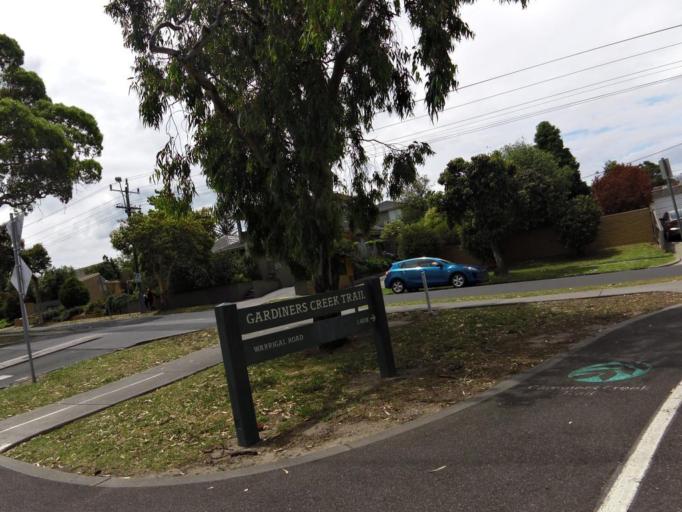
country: AU
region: Victoria
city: Ashburton
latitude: -37.8695
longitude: 145.0794
